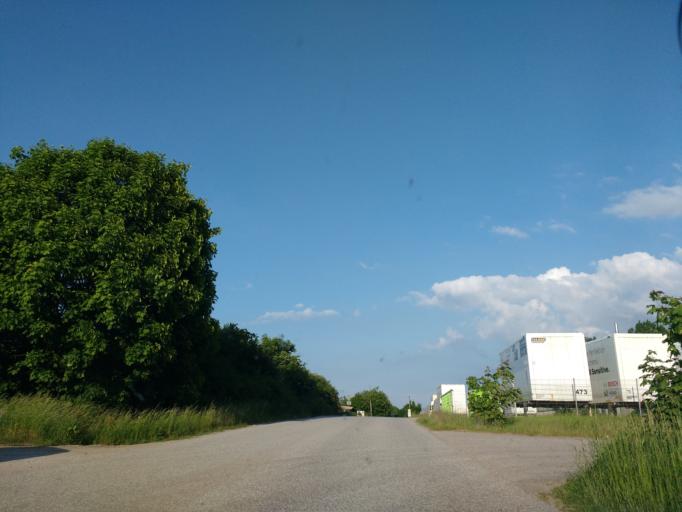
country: DE
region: Mecklenburg-Vorpommern
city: Zurow
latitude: 53.8631
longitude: 11.6197
